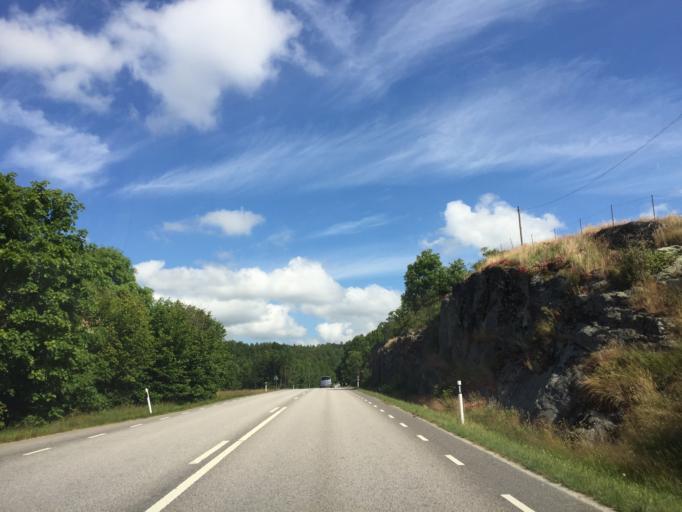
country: SE
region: Vaestra Goetaland
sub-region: Orust
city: Henan
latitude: 58.2747
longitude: 11.6938
